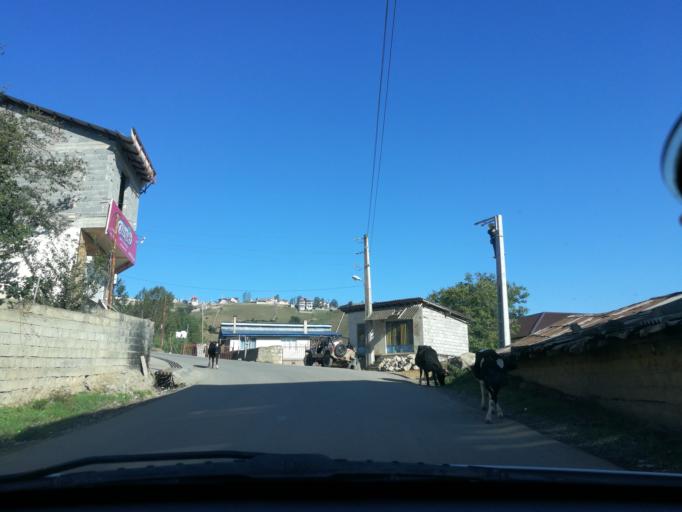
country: IR
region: Mazandaran
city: `Abbasabad
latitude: 36.5532
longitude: 51.1913
